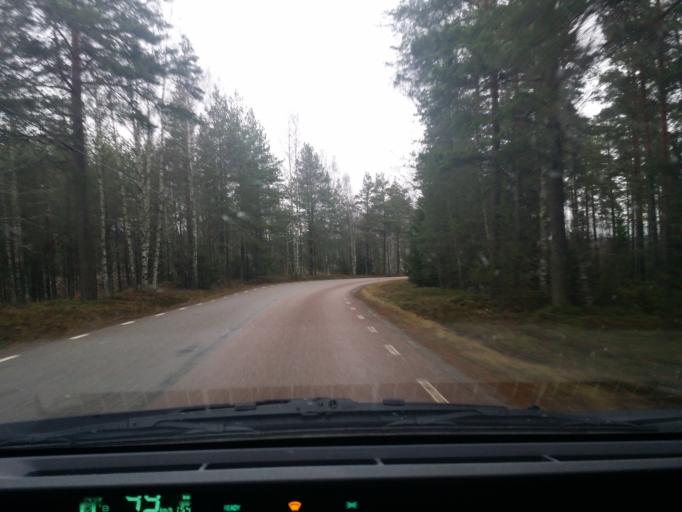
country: SE
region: Vaestmanland
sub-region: Sala Kommun
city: Sala
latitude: 59.8285
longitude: 16.5259
